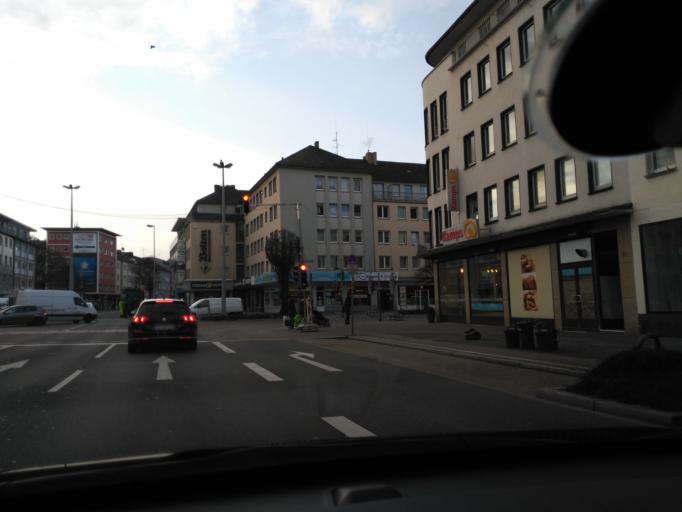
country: DE
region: North Rhine-Westphalia
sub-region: Regierungsbezirk Dusseldorf
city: Monchengladbach
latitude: 51.1668
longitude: 6.4471
